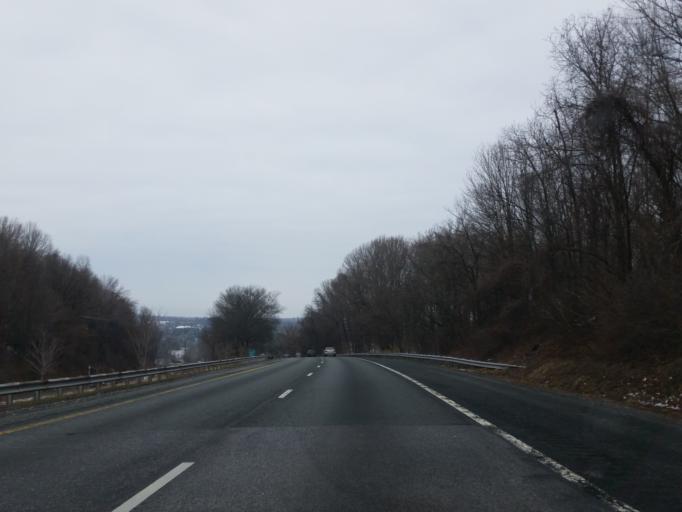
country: US
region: Maryland
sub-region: Baltimore County
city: Hunt Valley
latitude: 39.5274
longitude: -76.6606
